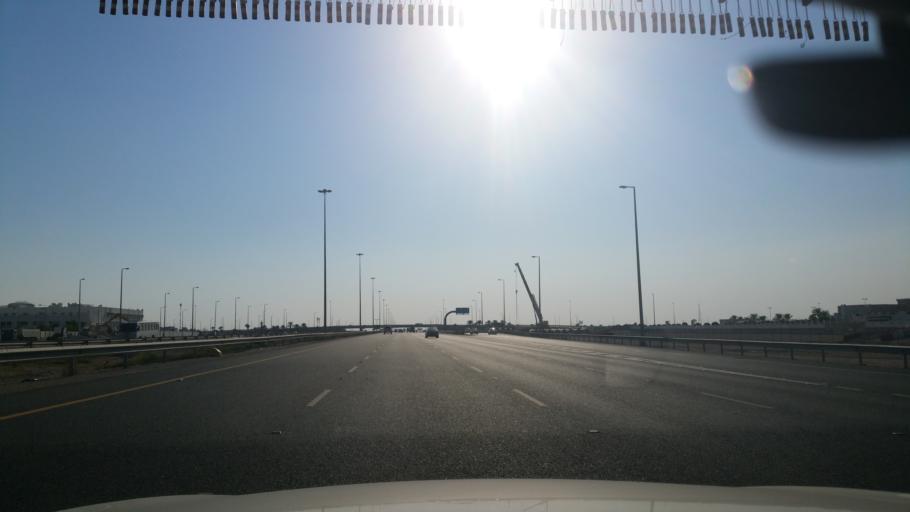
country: QA
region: Baladiyat ar Rayyan
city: Ar Rayyan
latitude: 25.2153
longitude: 51.4138
